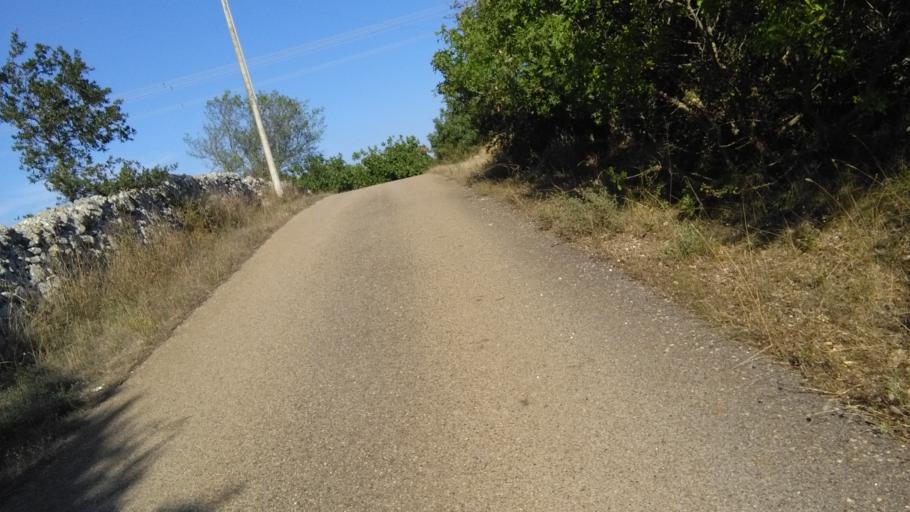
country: IT
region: Apulia
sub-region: Provincia di Bari
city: Putignano
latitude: 40.8194
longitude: 17.0493
